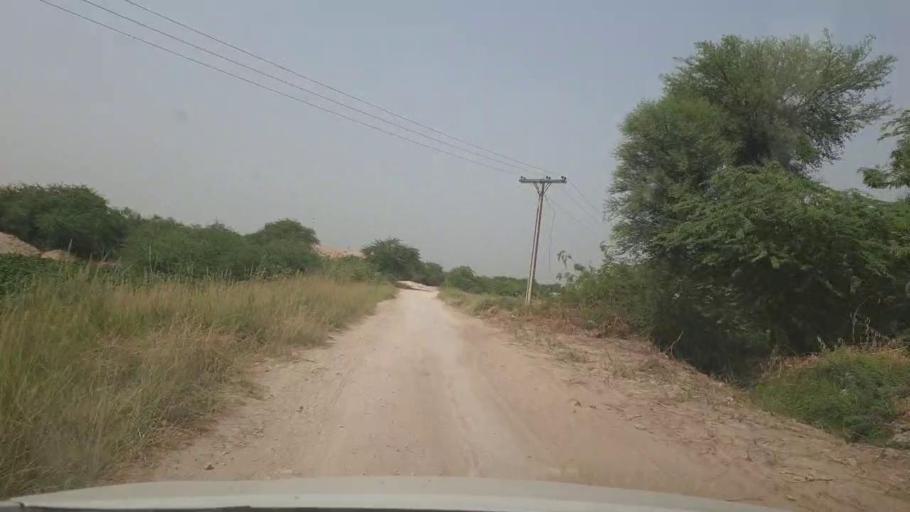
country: PK
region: Sindh
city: Kot Diji
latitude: 27.3075
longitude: 68.6905
